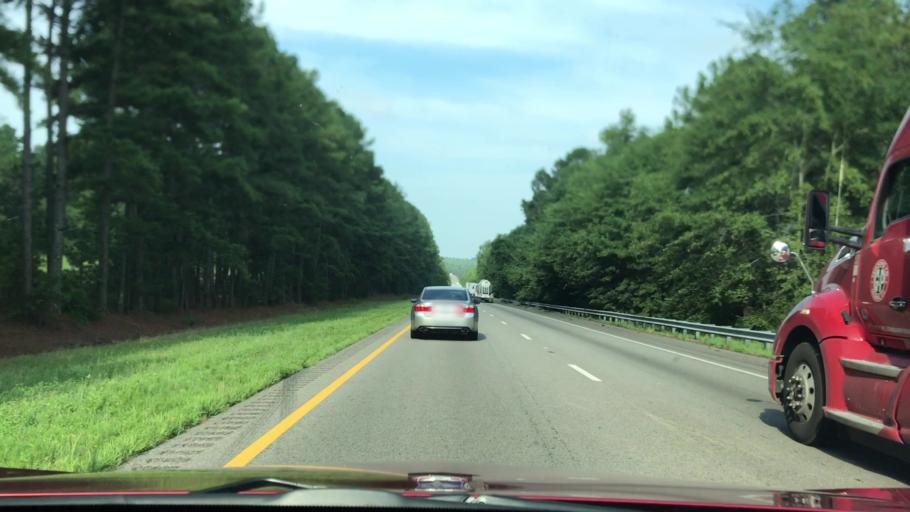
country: US
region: South Carolina
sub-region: Aiken County
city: Graniteville
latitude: 33.6312
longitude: -81.7969
